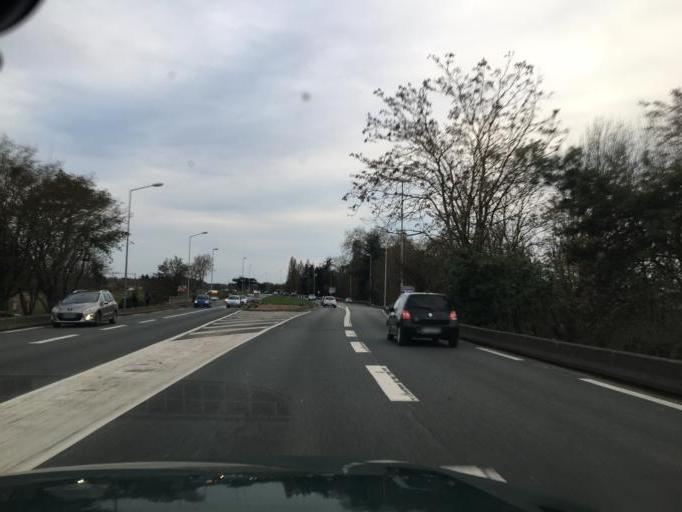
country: FR
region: Centre
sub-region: Departement du Loiret
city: Saint-Jean-le-Blanc
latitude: 47.8941
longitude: 1.9217
